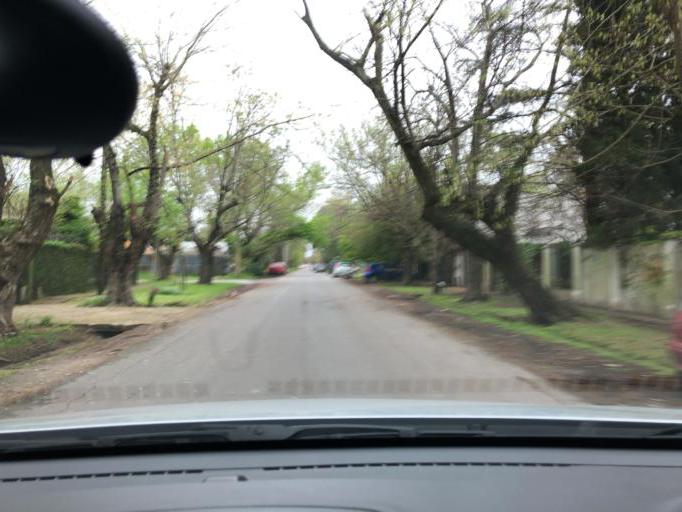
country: AR
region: Buenos Aires
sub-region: Partido de La Plata
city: La Plata
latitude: -34.8700
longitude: -58.0424
